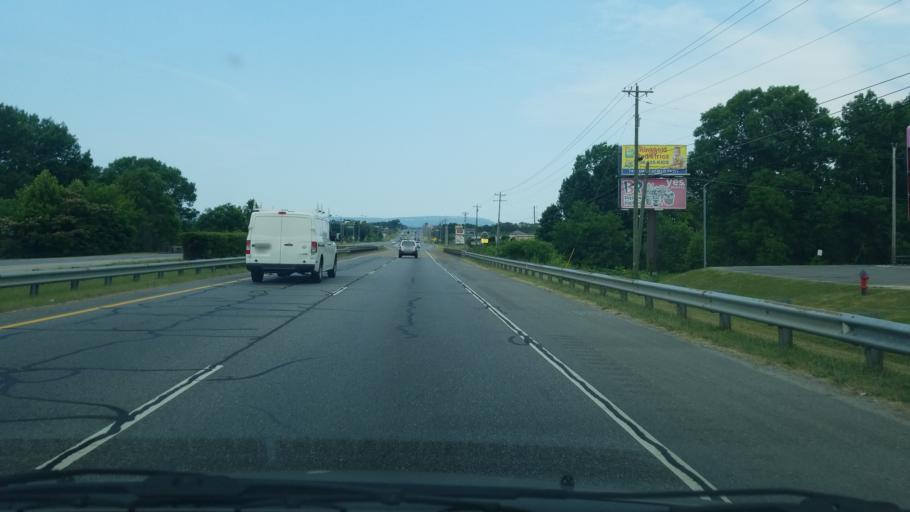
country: US
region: Georgia
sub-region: Catoosa County
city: Fort Oglethorpe
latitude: 34.9409
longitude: -85.2186
